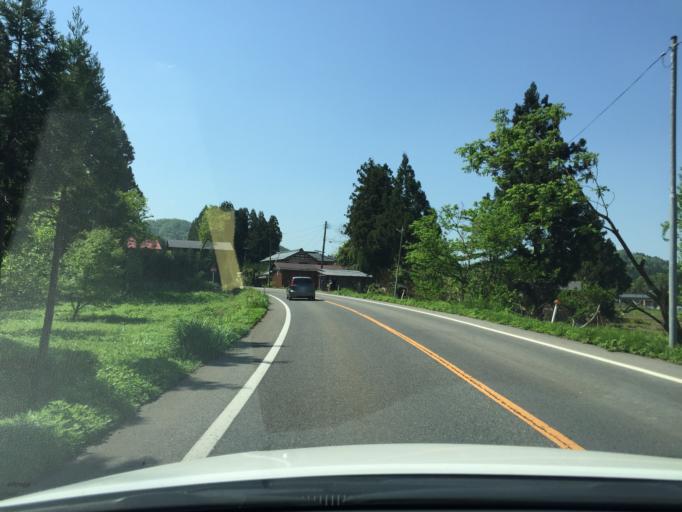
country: JP
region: Niigata
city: Muramatsu
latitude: 37.6638
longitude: 139.1380
